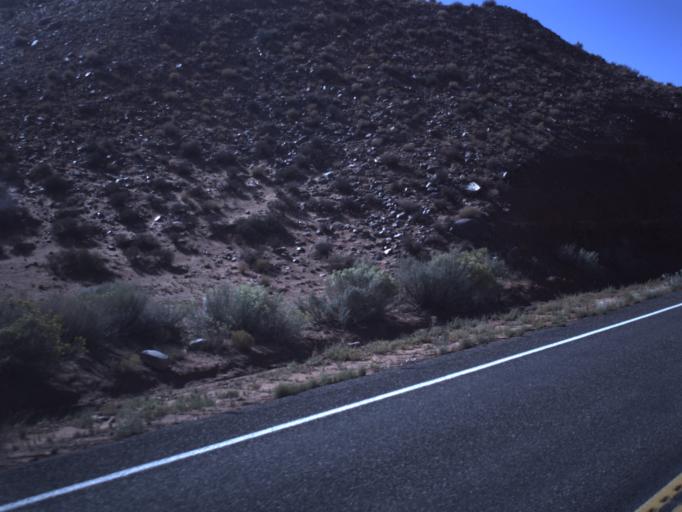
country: US
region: Utah
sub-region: Wayne County
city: Loa
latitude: 38.1444
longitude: -110.6125
